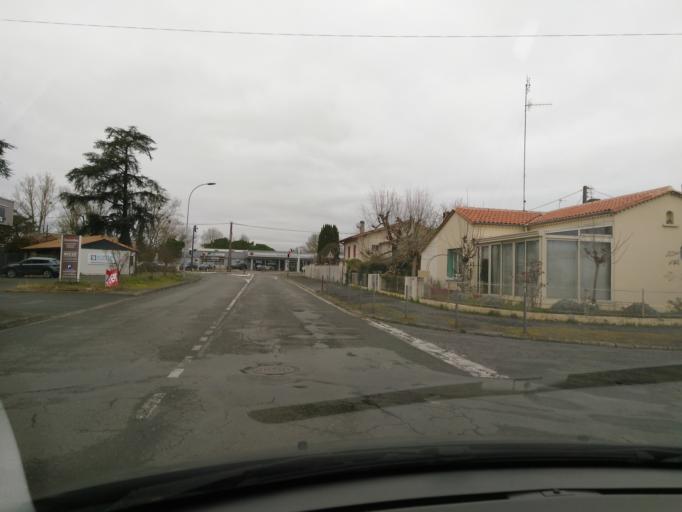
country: FR
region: Aquitaine
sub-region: Departement de la Dordogne
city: Bergerac
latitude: 44.8446
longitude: 0.4738
